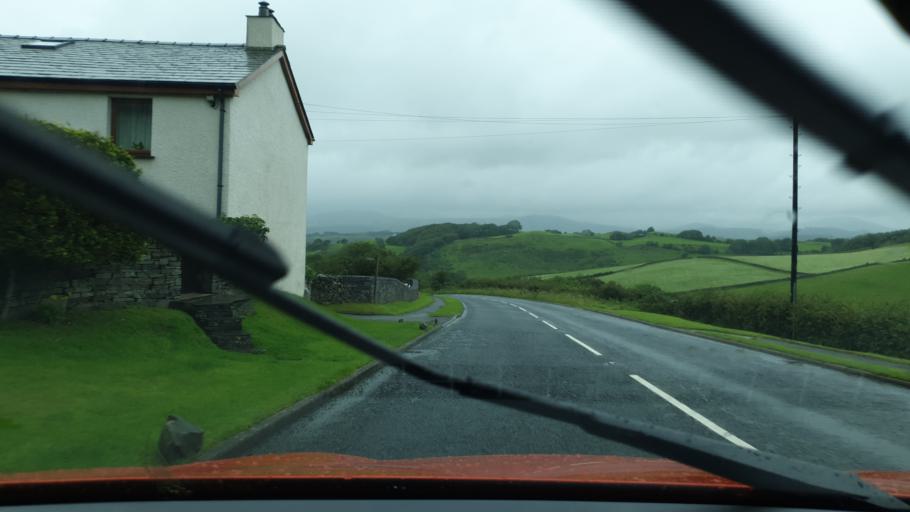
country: GB
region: England
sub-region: Cumbria
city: Ulverston
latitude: 54.2544
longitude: -3.1625
